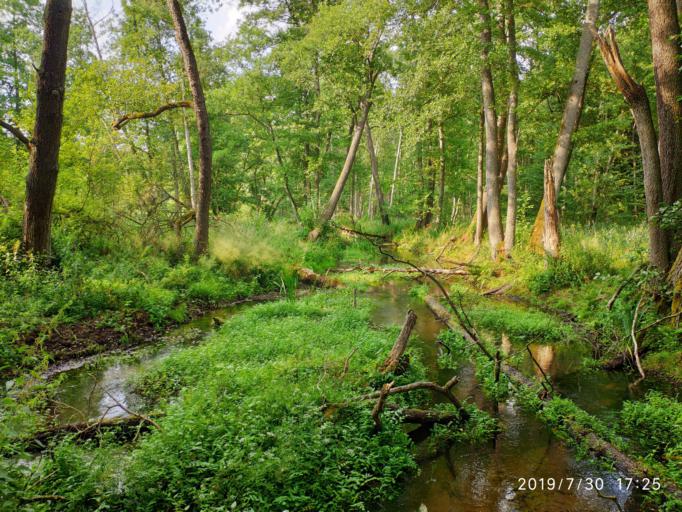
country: PL
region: Lubusz
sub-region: Powiat krosnienski
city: Bytnica
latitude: 52.1611
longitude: 15.2700
